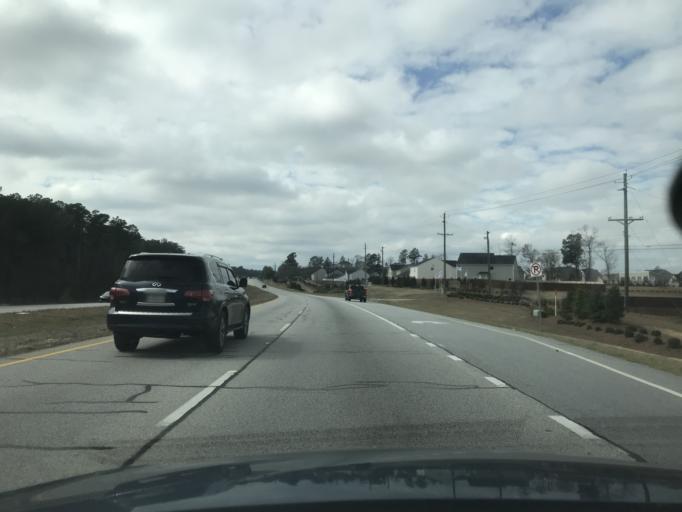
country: US
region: Georgia
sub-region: Columbia County
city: Grovetown
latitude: 33.4387
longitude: -82.1403
